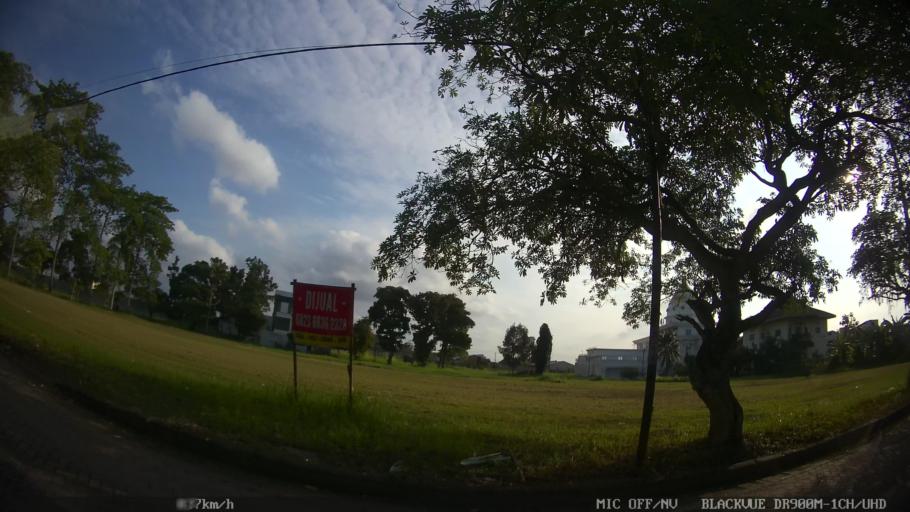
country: ID
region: North Sumatra
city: Medan
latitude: 3.6206
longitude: 98.6513
